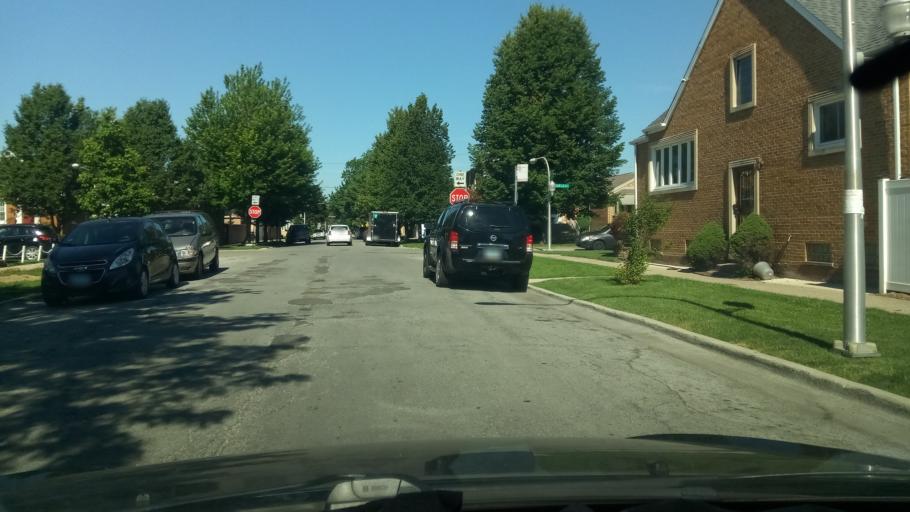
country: US
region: Illinois
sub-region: Cook County
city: Hometown
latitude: 41.7697
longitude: -87.7241
